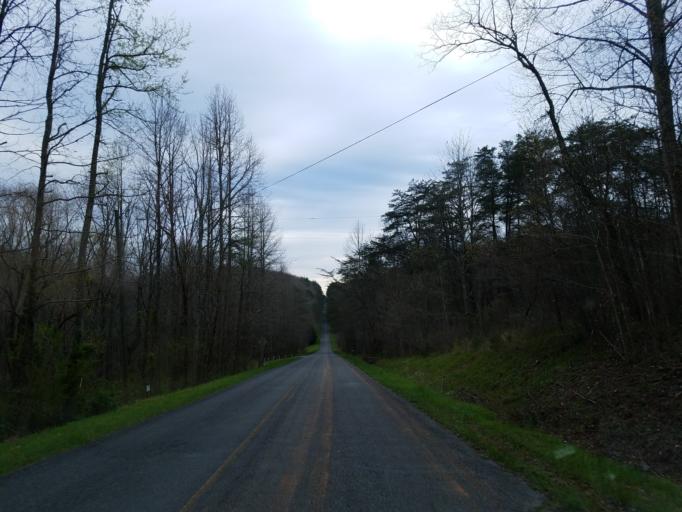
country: US
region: Georgia
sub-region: Fannin County
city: Blue Ridge
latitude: 34.7033
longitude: -84.2939
